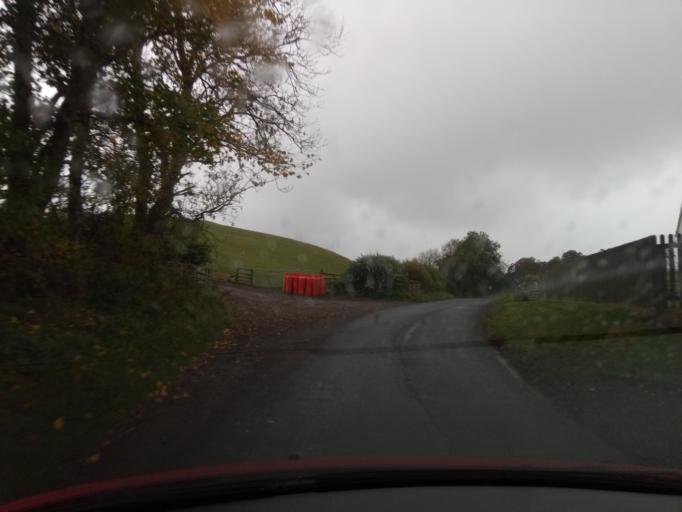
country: GB
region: Scotland
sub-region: The Scottish Borders
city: Selkirk
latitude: 55.5123
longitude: -2.7881
